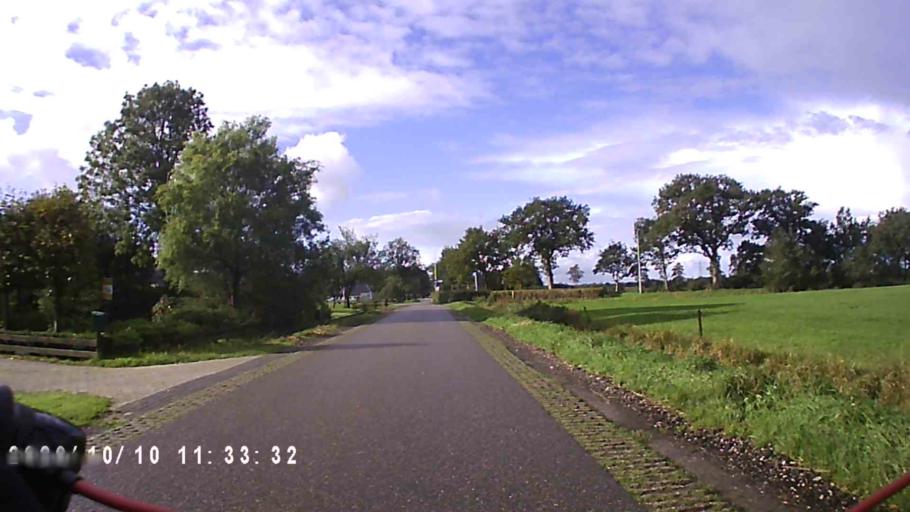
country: NL
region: Friesland
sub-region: Gemeente Smallingerland
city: Drachten
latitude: 53.0804
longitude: 6.1297
